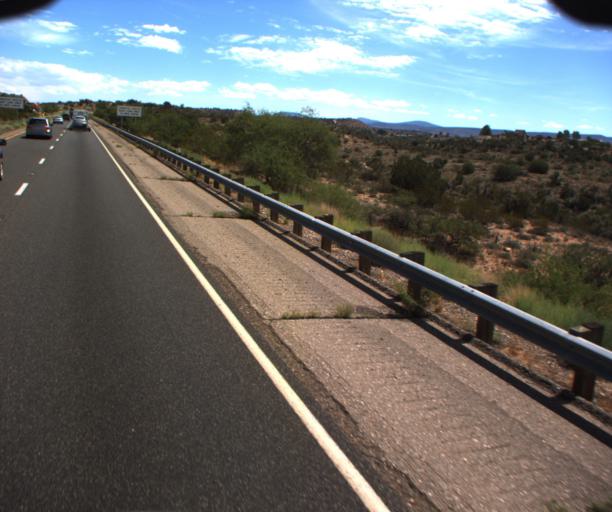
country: US
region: Arizona
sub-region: Yavapai County
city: Lake Montezuma
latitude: 34.6511
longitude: -111.7985
